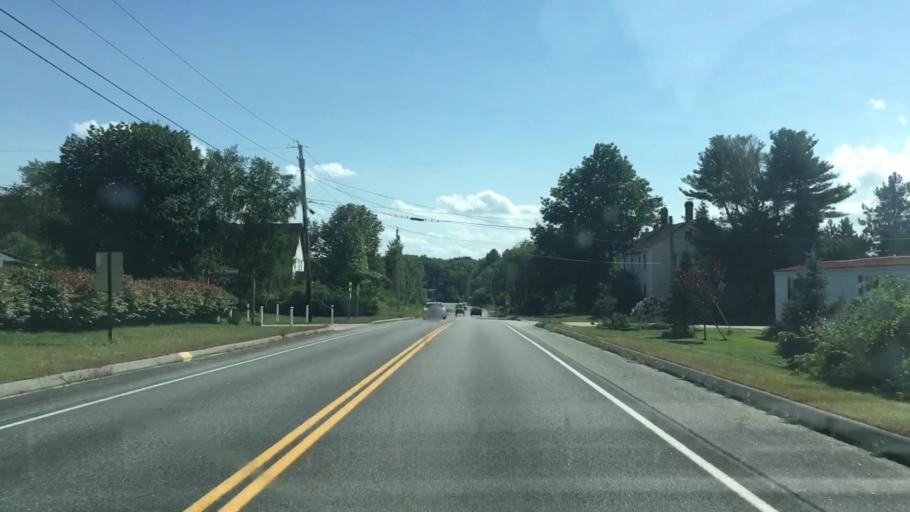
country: US
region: Maine
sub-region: Androscoggin County
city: Lisbon
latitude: 44.0604
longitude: -70.0857
